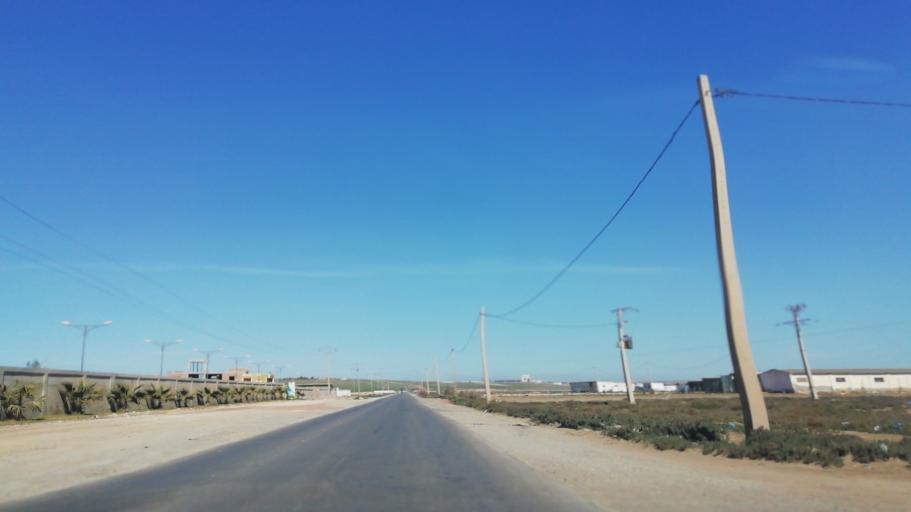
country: DZ
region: Oran
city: Es Senia
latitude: 35.5207
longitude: -0.5882
